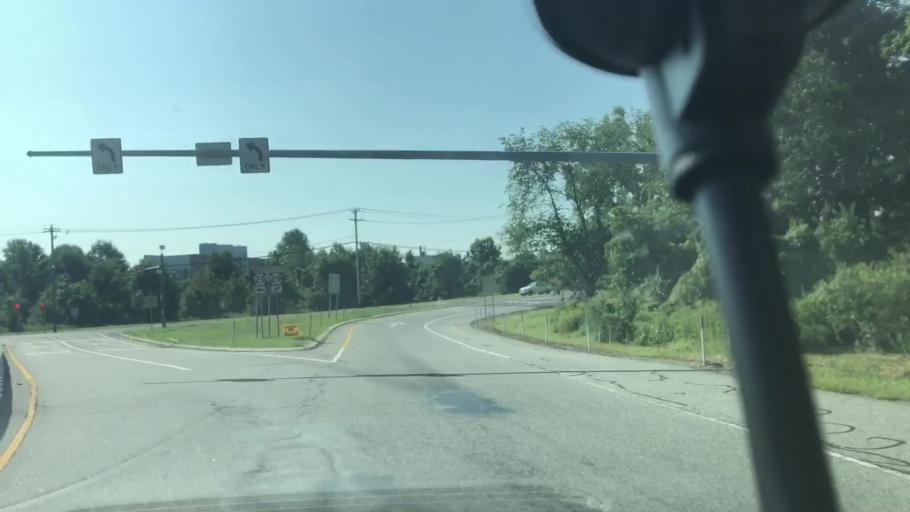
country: US
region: Pennsylvania
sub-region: Montgomery County
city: Trappe
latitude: 40.1603
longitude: -75.4823
